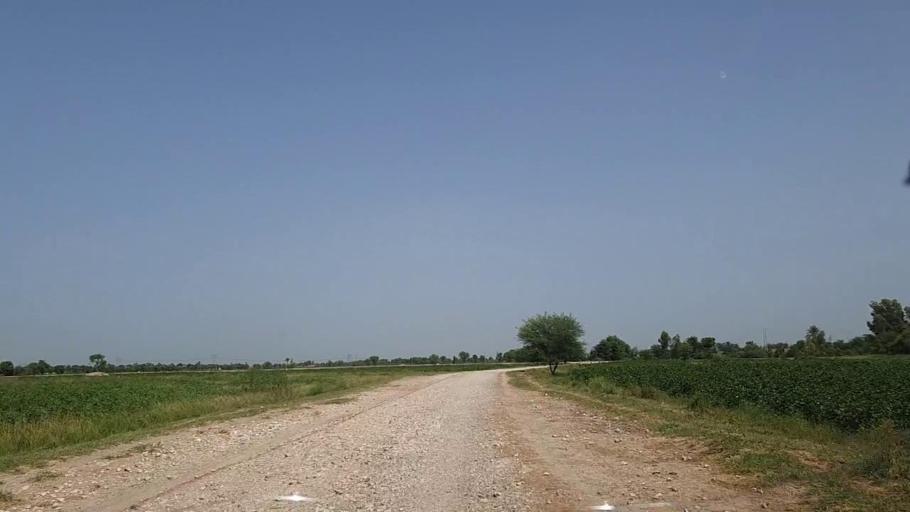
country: PK
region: Sindh
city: Kandiaro
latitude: 27.0132
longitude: 68.1713
